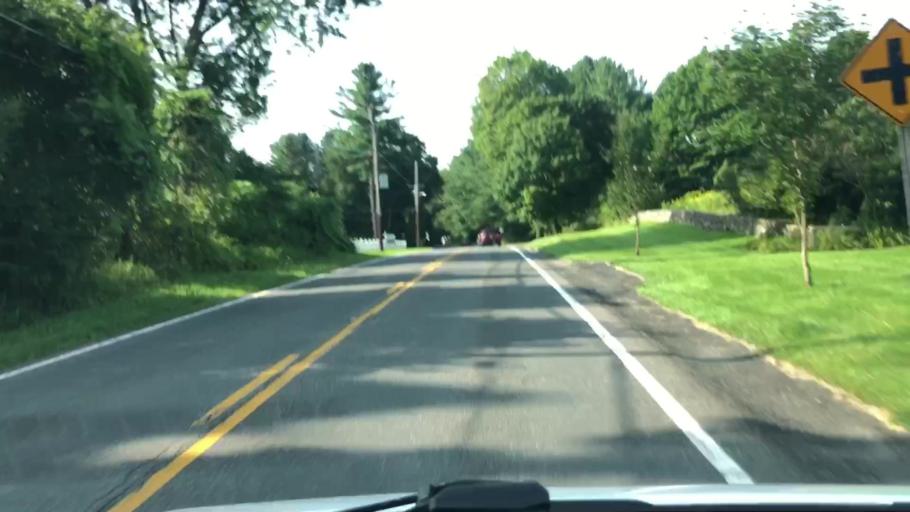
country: US
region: Massachusetts
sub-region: Berkshire County
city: Stockbridge
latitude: 42.3040
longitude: -73.2938
